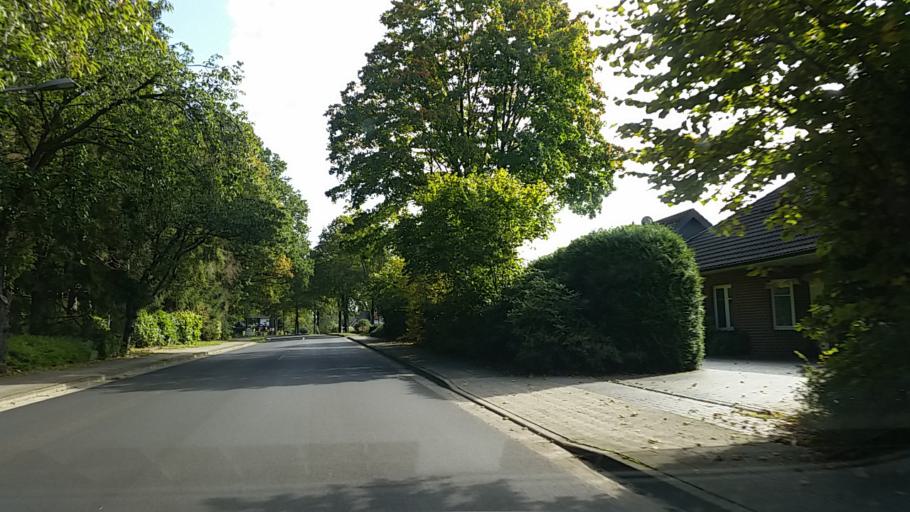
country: DE
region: Lower Saxony
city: Neuenkirchen
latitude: 53.0307
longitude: 9.7105
